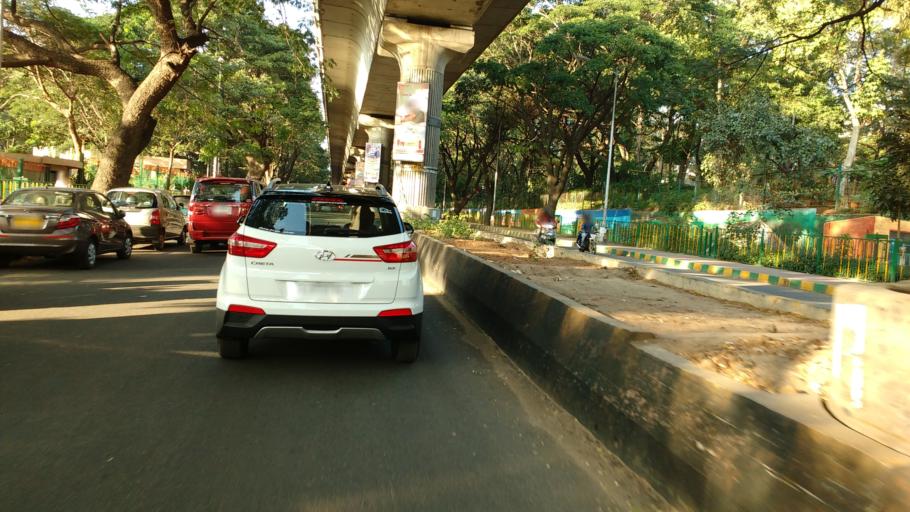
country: IN
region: Karnataka
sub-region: Bangalore Urban
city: Bangalore
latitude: 12.9344
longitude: 77.5801
